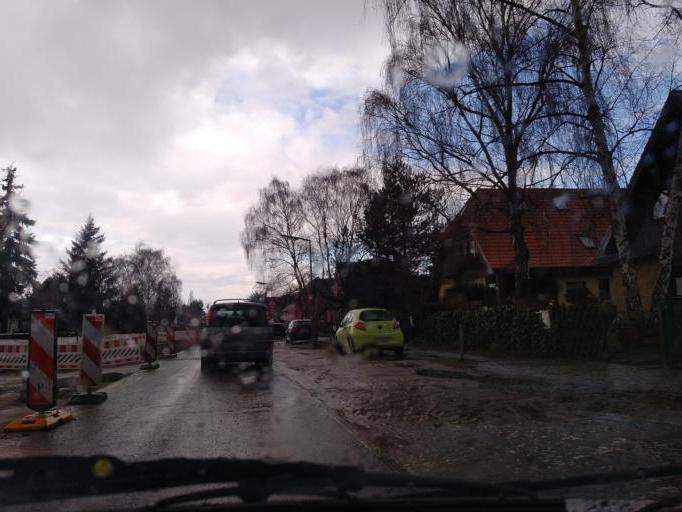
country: DE
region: Berlin
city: Staaken
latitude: 52.5436
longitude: 13.1556
